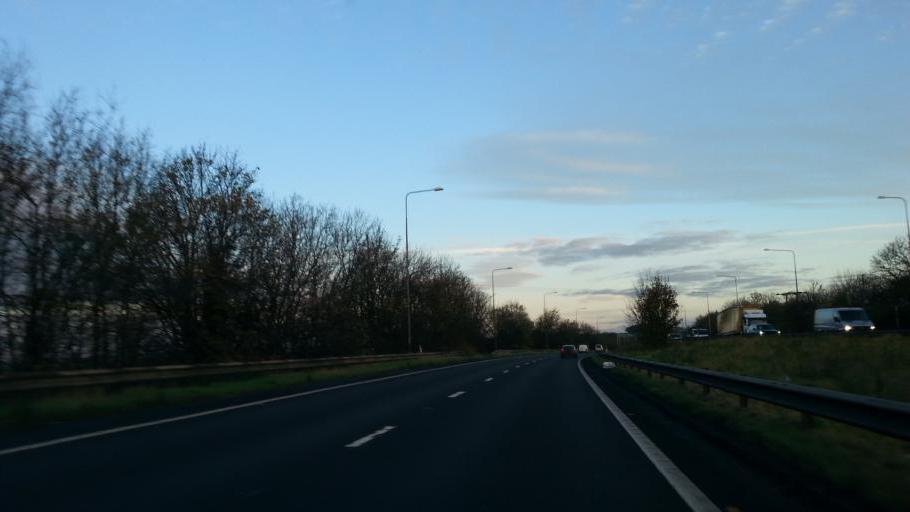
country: GB
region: England
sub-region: Doncaster
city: Carcroft
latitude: 53.5932
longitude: -1.2162
